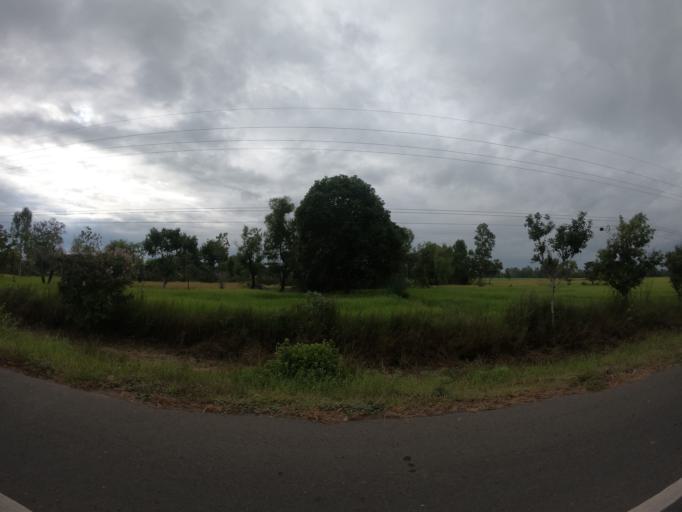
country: TH
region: Roi Et
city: Thawat Buri
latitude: 16.0864
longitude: 103.7556
